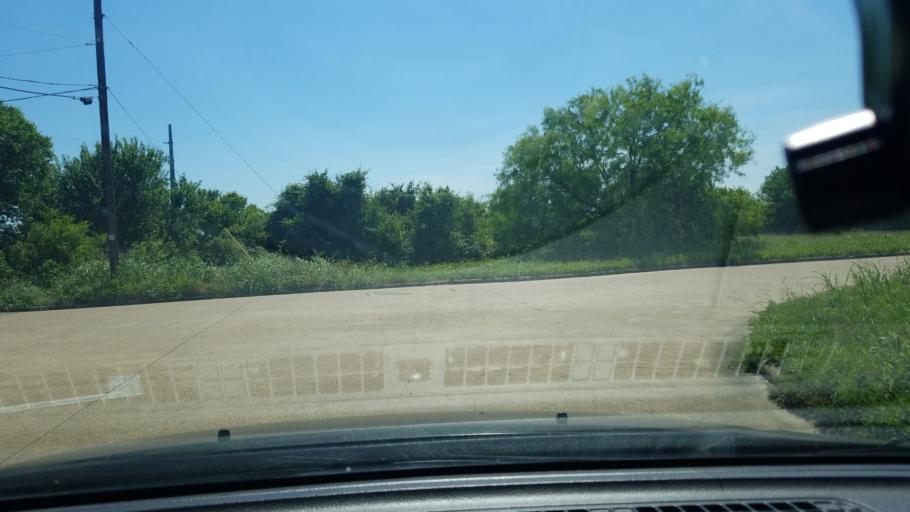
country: US
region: Texas
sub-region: Dallas County
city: Mesquite
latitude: 32.7753
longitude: -96.6215
